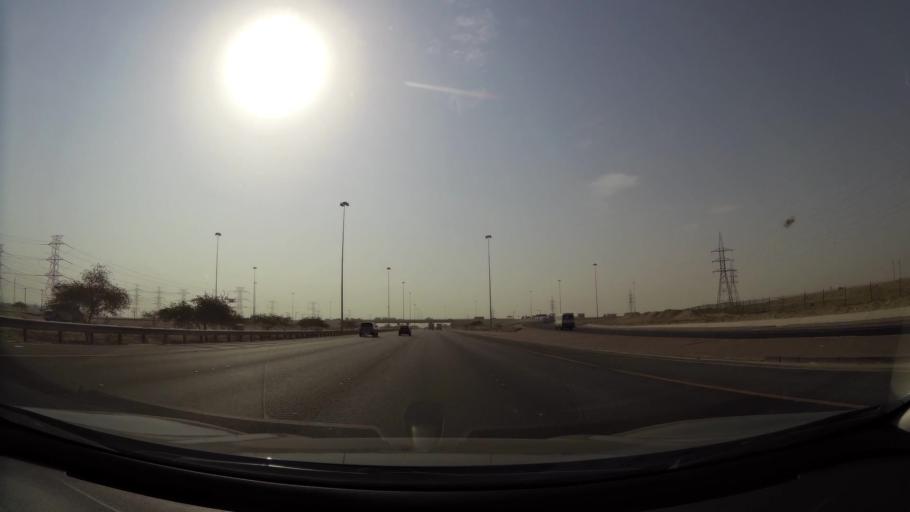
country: KW
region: Al Ahmadi
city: Al Ahmadi
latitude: 28.9943
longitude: 48.1002
